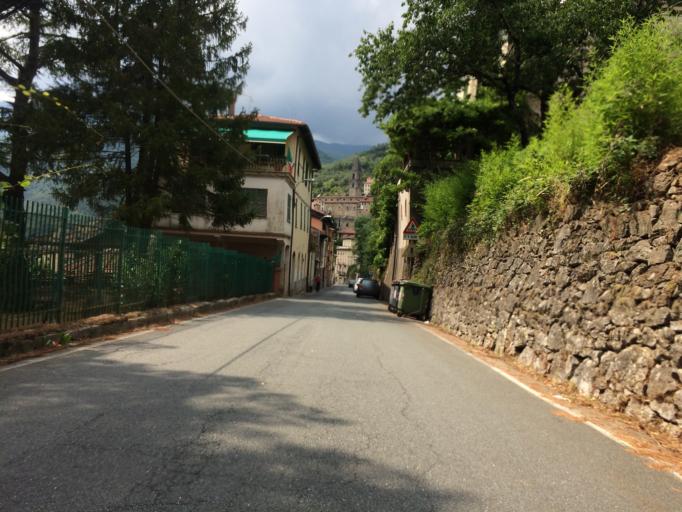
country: IT
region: Liguria
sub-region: Provincia di Imperia
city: Pigna
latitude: 43.9314
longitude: 7.6677
